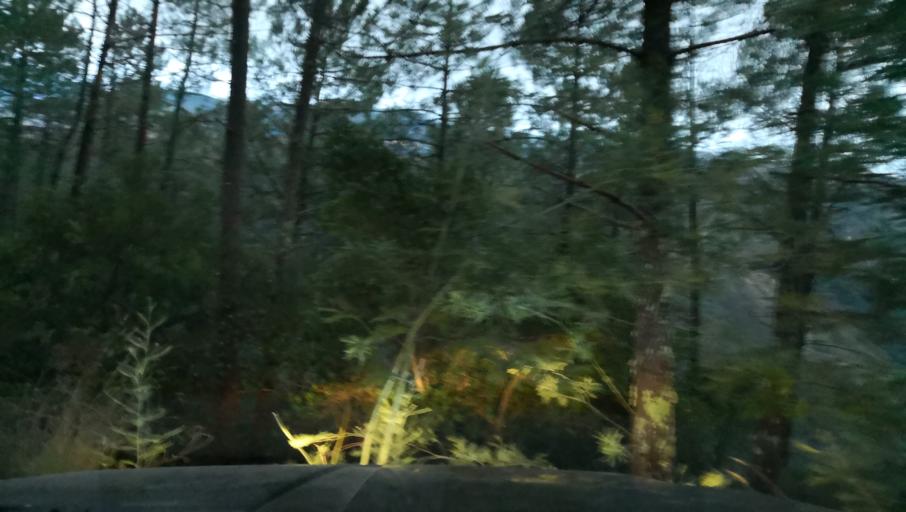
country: PT
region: Vila Real
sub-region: Vila Real
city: Vila Real
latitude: 41.2628
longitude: -7.7436
